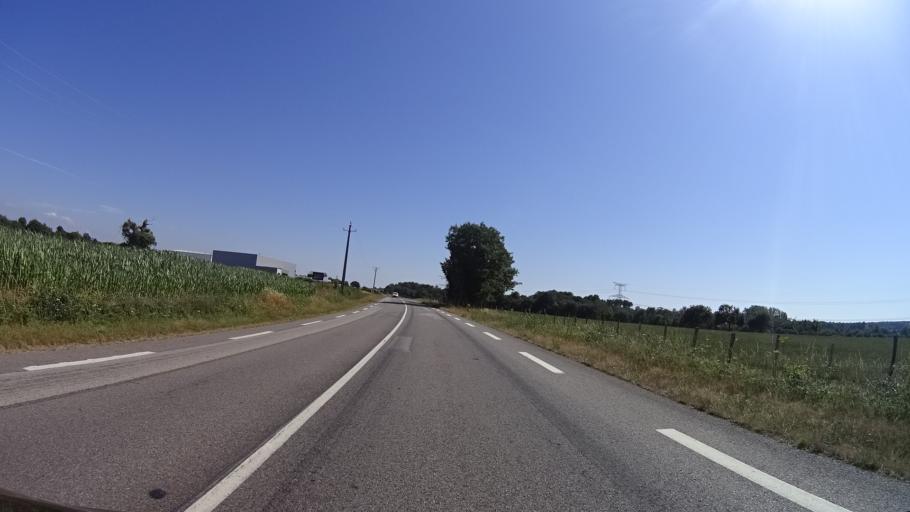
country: FR
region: Brittany
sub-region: Departement du Morbihan
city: Saint-Dolay
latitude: 47.5681
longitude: -2.1315
